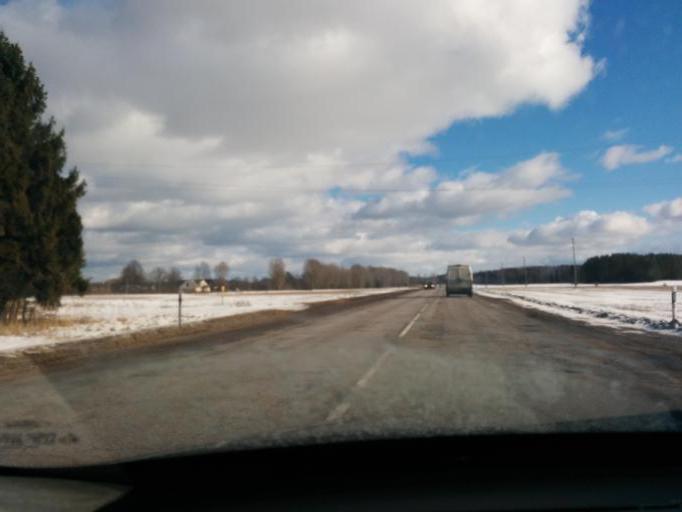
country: LV
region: Cesvaine
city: Cesvaine
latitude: 57.2387
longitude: 26.4055
